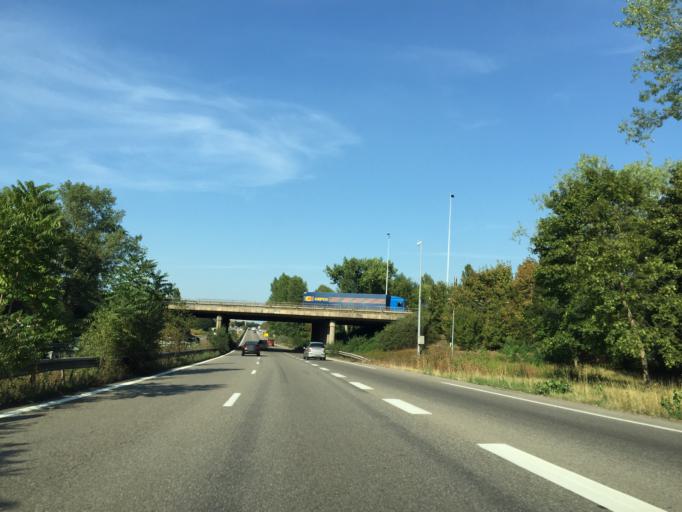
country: FR
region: Alsace
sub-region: Departement du Bas-Rhin
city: Illkirch-Graffenstaden
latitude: 48.5294
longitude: 7.6924
